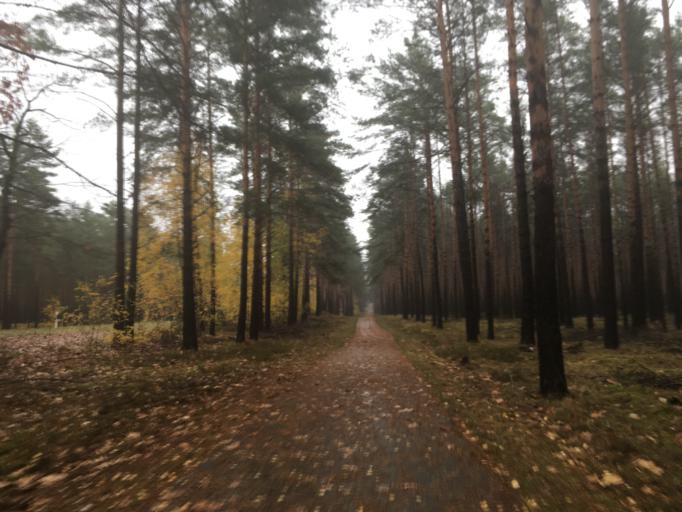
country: DE
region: Brandenburg
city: Schlepzig
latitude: 52.0325
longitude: 13.8062
